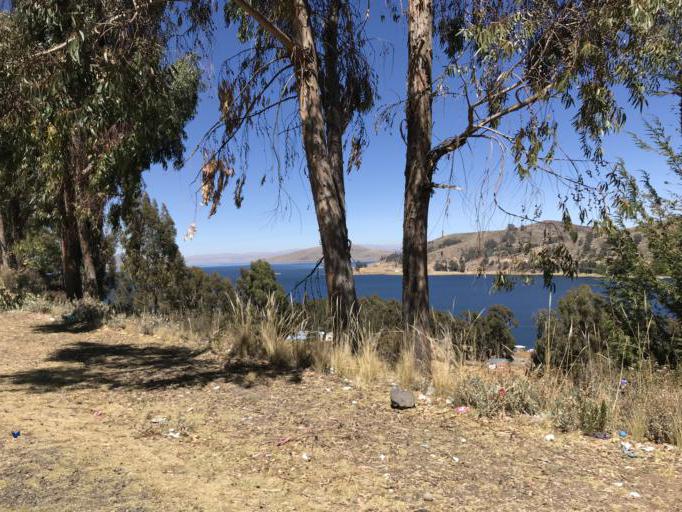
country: BO
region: La Paz
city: San Pablo
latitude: -16.2179
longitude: -68.8368
